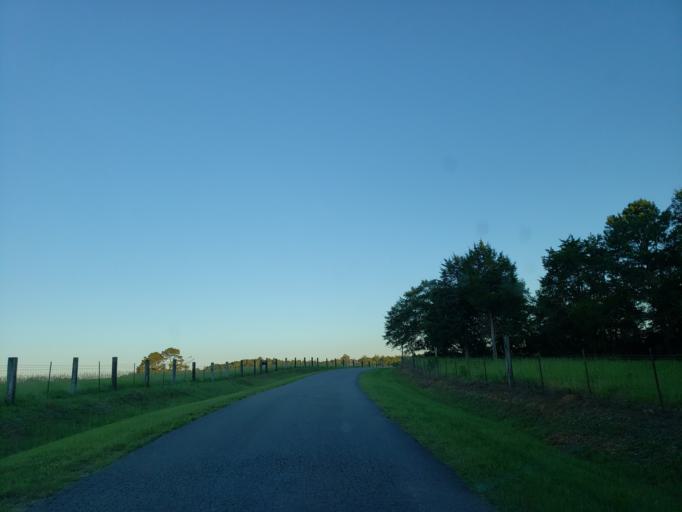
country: US
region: Georgia
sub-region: Bartow County
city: Euharlee
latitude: 34.1019
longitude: -84.8761
